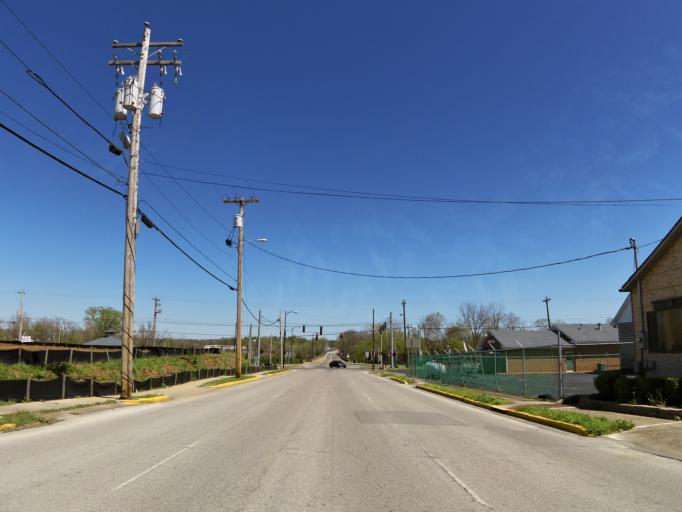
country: US
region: Kentucky
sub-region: Warren County
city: Bowling Green
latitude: 36.9993
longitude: -86.4306
